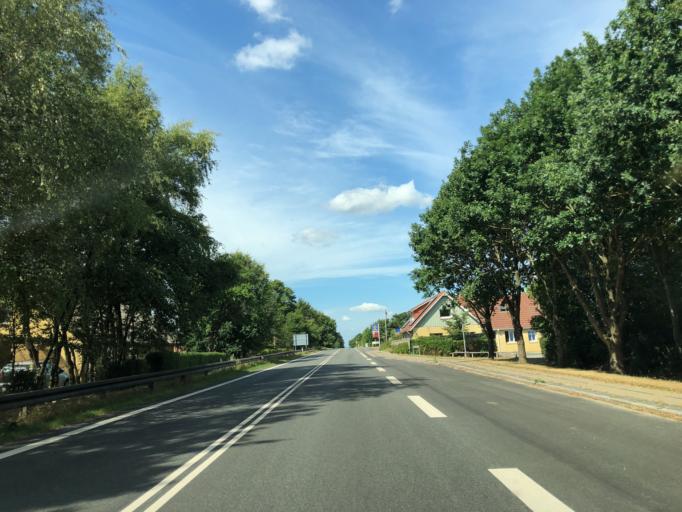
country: DK
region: Central Jutland
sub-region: Ikast-Brande Kommune
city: Bording Kirkeby
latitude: 56.1400
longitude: 9.2880
